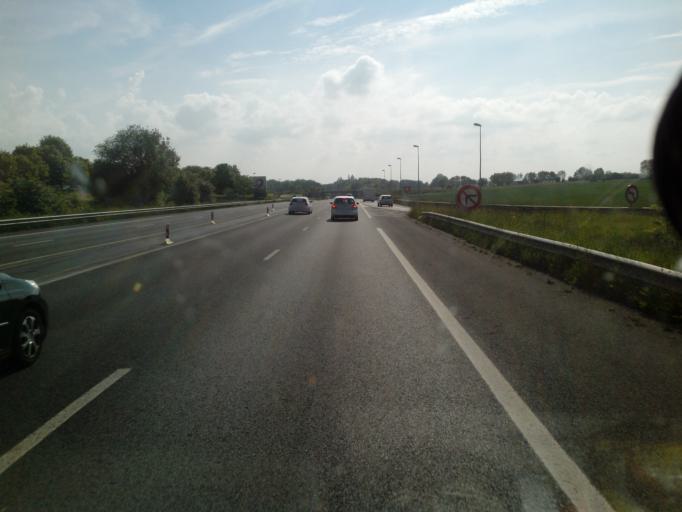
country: FR
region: Haute-Normandie
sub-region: Departement de la Seine-Maritime
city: Saint-Saens
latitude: 49.6768
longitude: 1.3356
